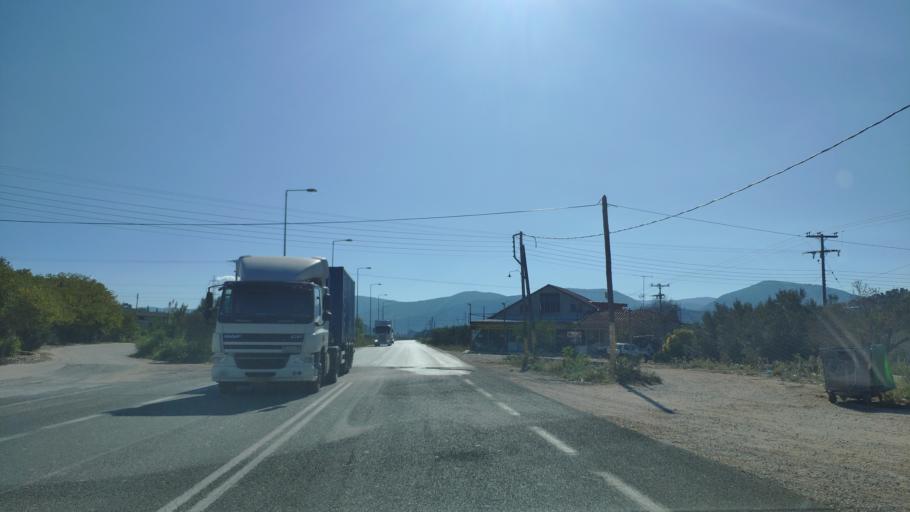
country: GR
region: Peloponnese
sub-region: Nomos Korinthias
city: Khiliomodhi
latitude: 37.8519
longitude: 22.8951
